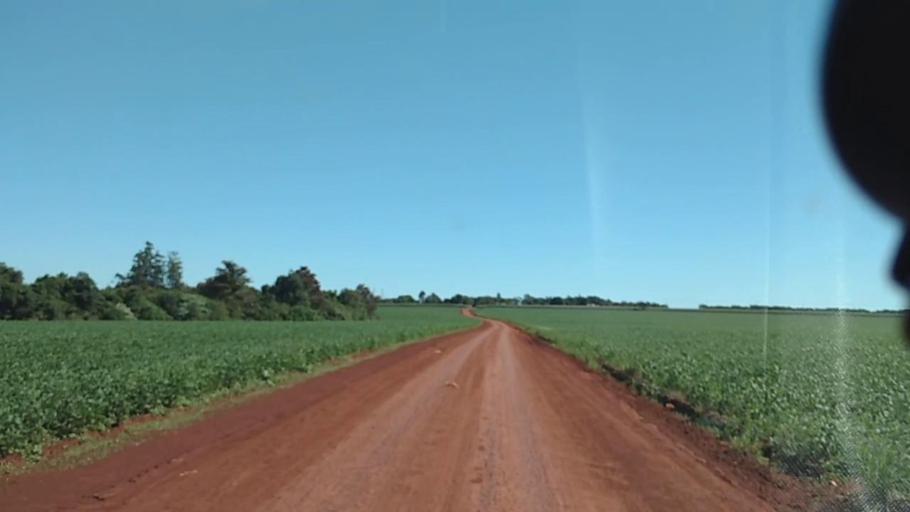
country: PY
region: Alto Parana
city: Naranjal
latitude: -25.9487
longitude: -55.1129
